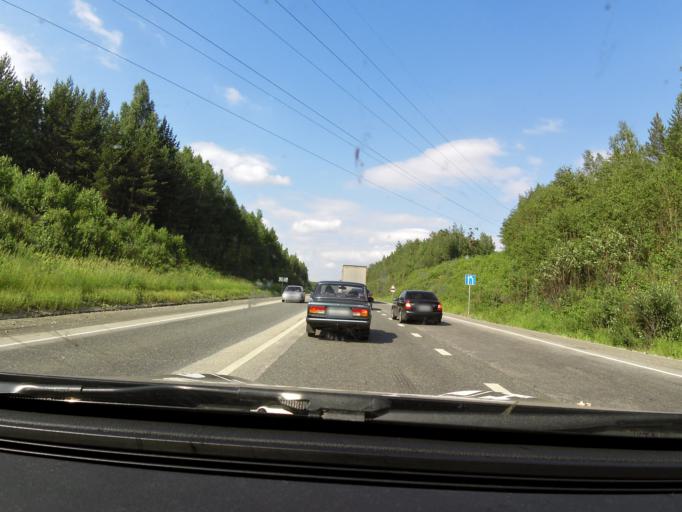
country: RU
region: Sverdlovsk
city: Talitsa
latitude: 56.8304
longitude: 59.9946
